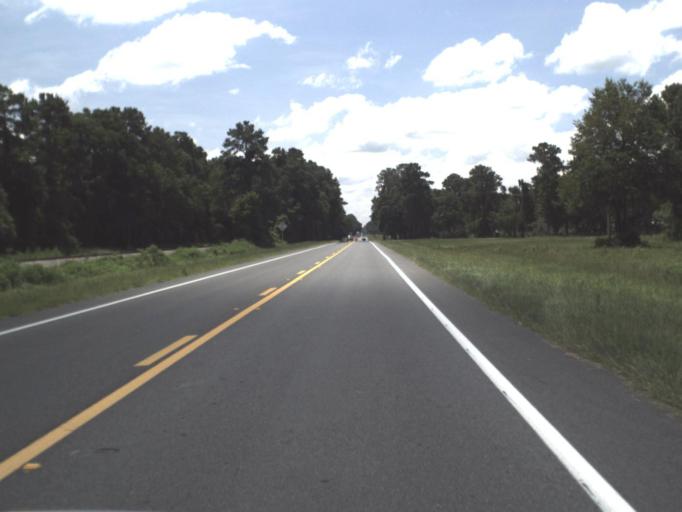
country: US
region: Florida
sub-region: Suwannee County
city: Wellborn
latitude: 30.3617
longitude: -82.7883
